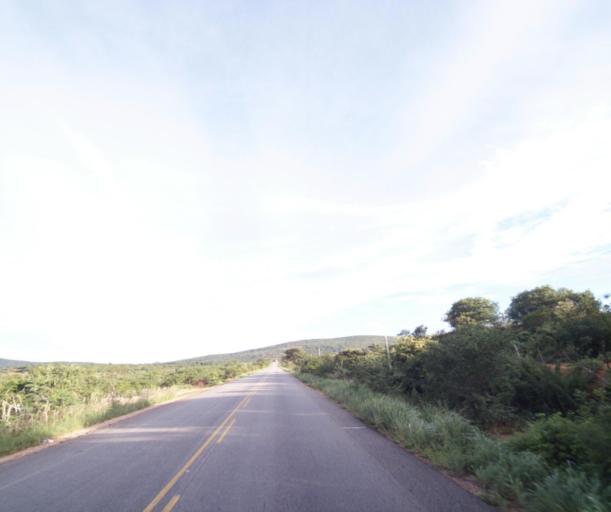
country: BR
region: Bahia
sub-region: Cacule
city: Cacule
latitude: -14.1825
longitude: -42.1652
